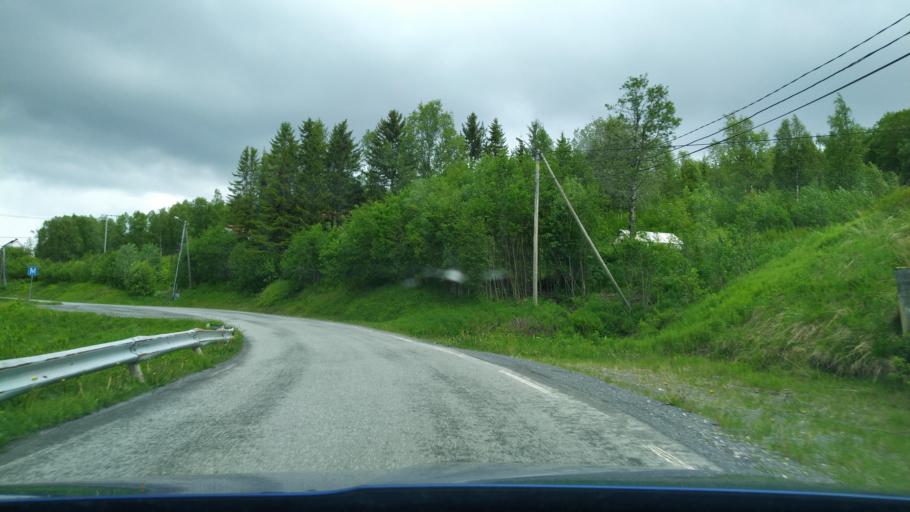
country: NO
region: Troms
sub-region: Tranoy
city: Vangsvika
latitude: 69.1261
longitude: 17.8541
